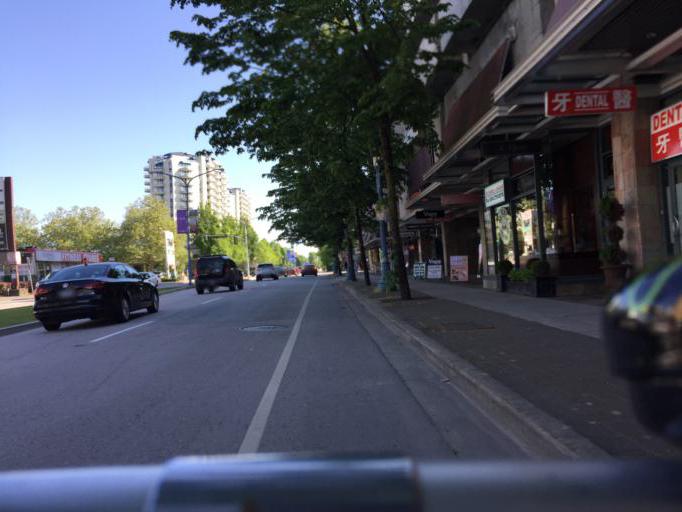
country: CA
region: British Columbia
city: Richmond
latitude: 49.1712
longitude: -123.1402
